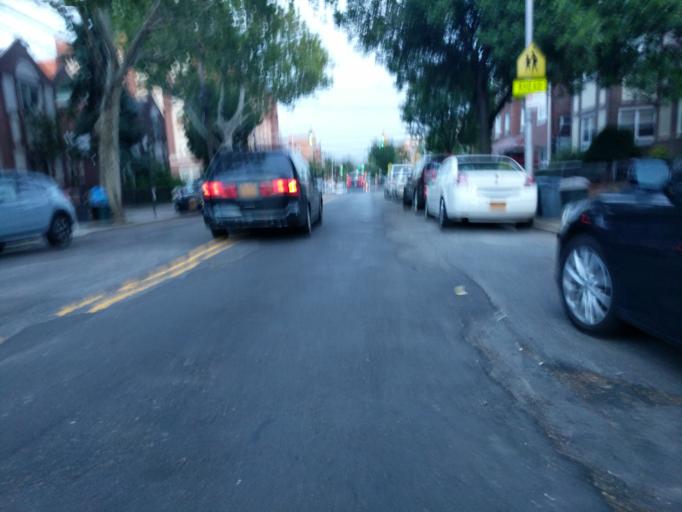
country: US
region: New York
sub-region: Queens County
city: Long Island City
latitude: 40.7760
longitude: -73.9058
